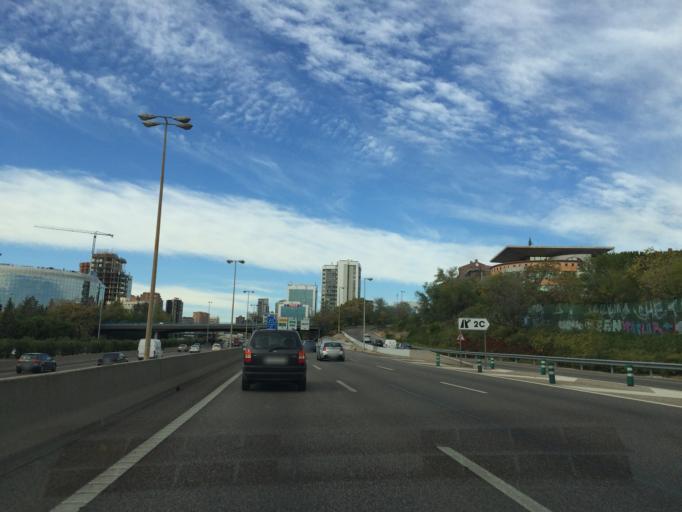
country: ES
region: Madrid
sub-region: Provincia de Madrid
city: Chamartin
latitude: 40.4648
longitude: -3.6671
